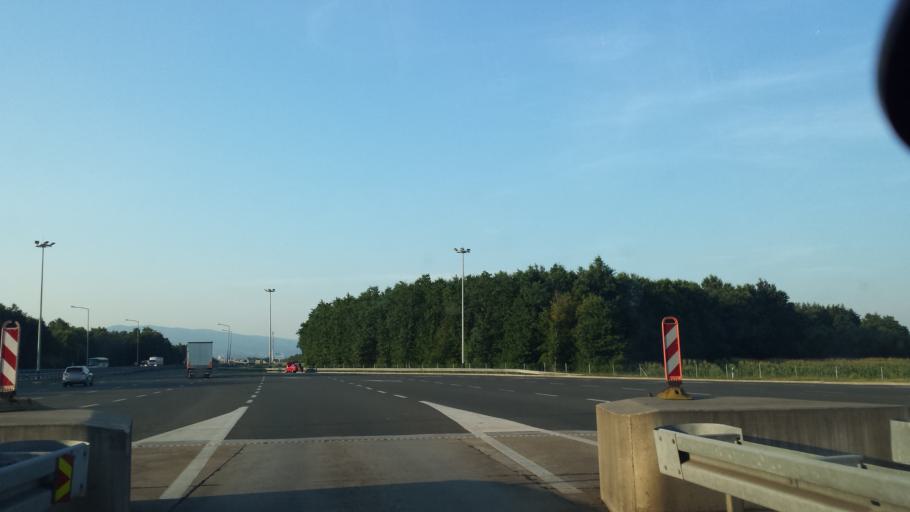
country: HR
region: Grad Zagreb
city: Brezovica
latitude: 45.7237
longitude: 15.8701
